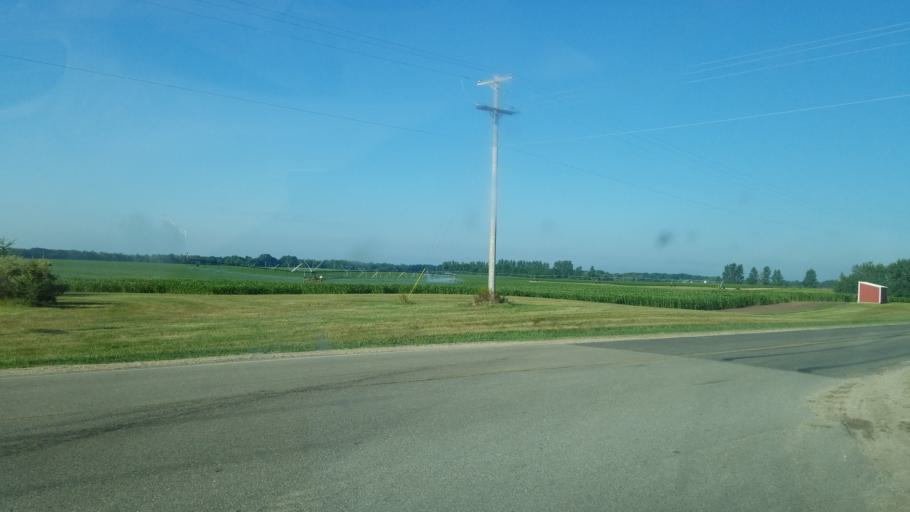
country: US
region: Michigan
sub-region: Montcalm County
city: Howard City
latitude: 43.4905
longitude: -85.3929
